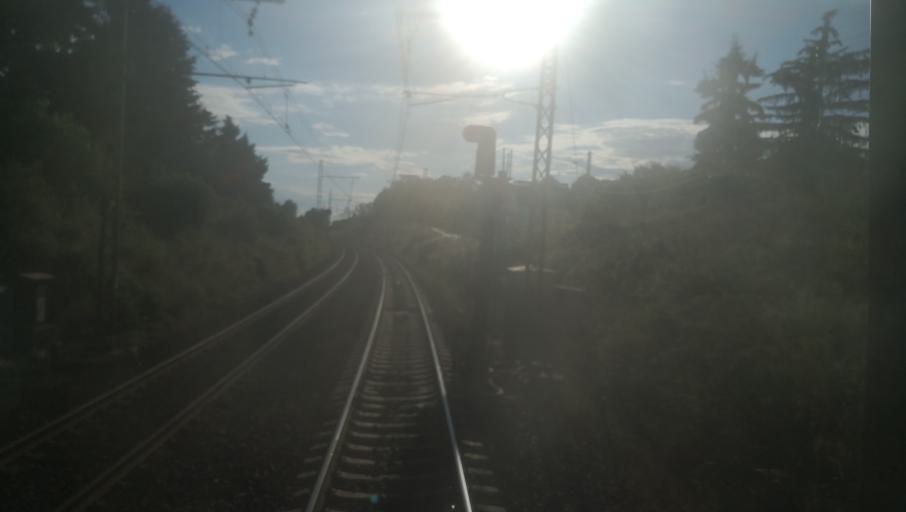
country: FR
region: Centre
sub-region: Departement du Cher
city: Vierzon
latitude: 47.2212
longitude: 2.0842
